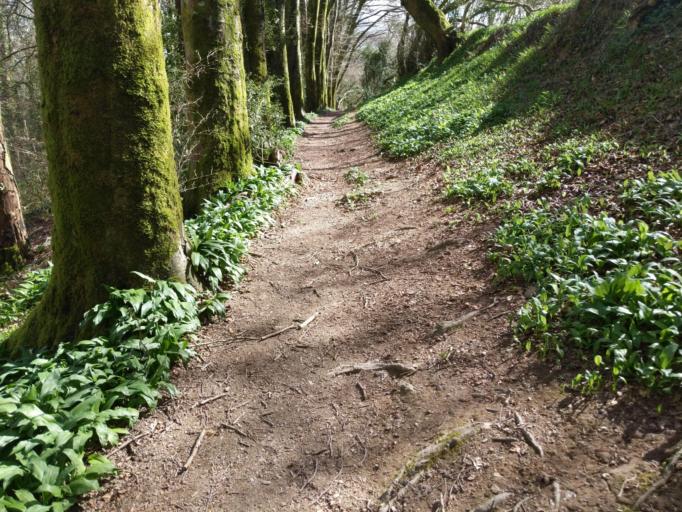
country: GB
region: England
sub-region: Plymouth
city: Plymouth
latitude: 50.4240
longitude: -4.1521
